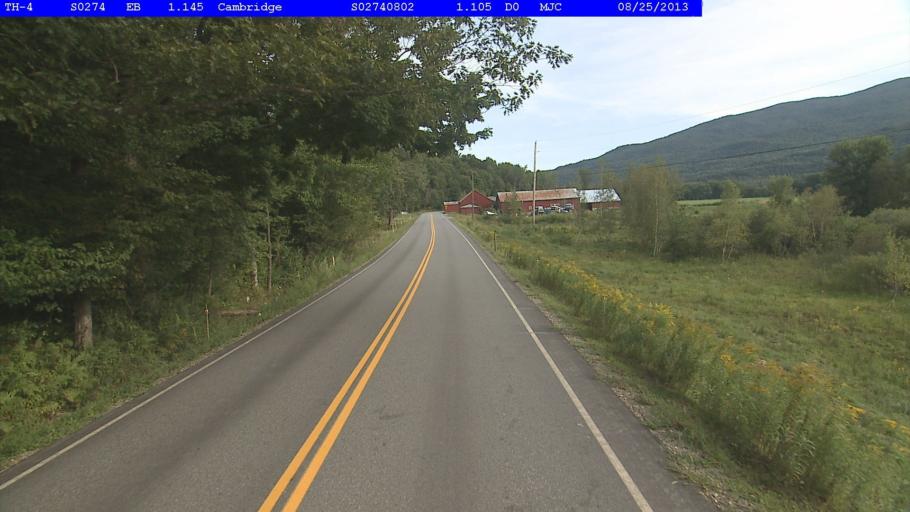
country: US
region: Vermont
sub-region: Lamoille County
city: Johnson
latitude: 44.6687
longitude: -72.7625
